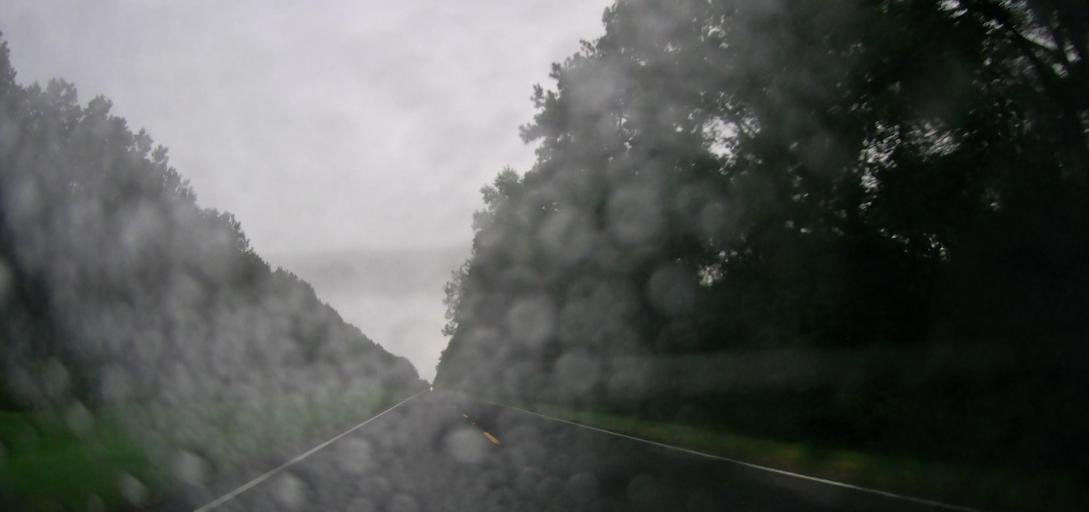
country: US
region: Georgia
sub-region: Glynn County
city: Dock Junction
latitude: 31.2636
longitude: -81.6290
